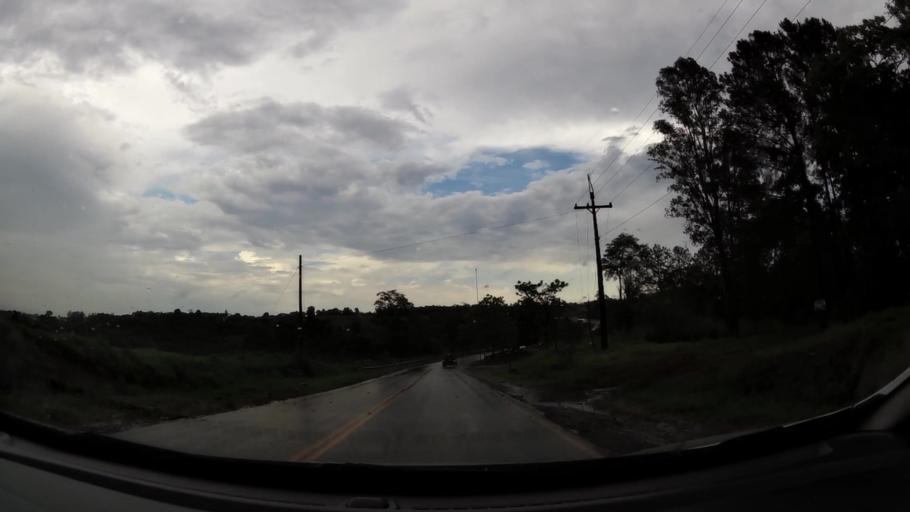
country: PY
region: Alto Parana
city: Los Cedrales
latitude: -25.5840
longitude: -54.6739
